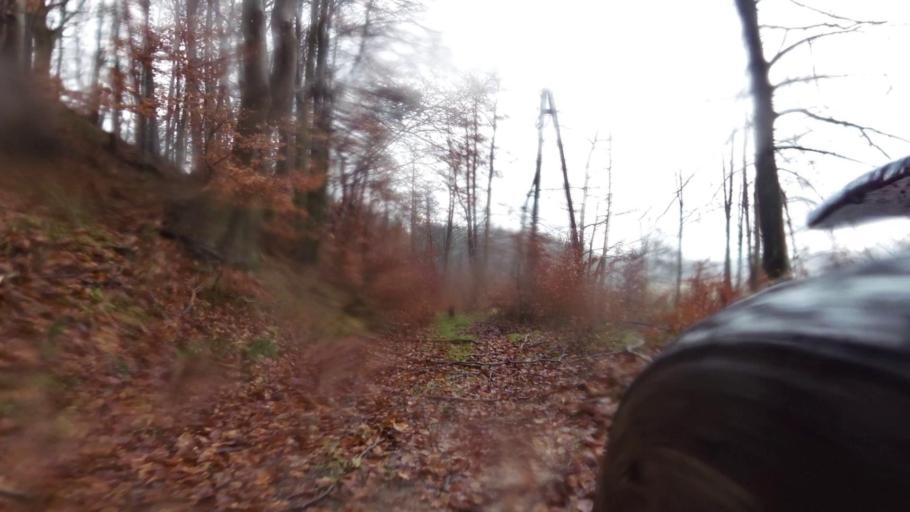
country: PL
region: West Pomeranian Voivodeship
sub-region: Powiat drawski
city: Czaplinek
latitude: 53.5847
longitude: 16.2618
